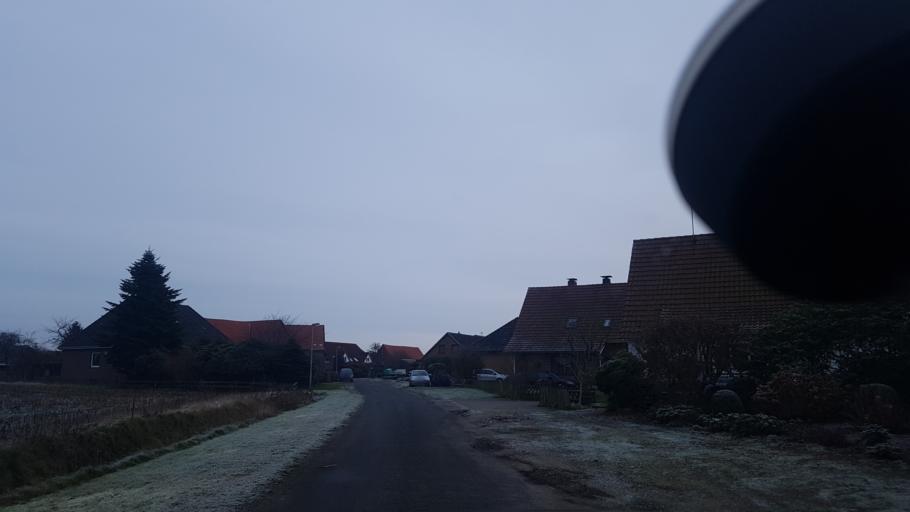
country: DE
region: Lower Saxony
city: Elmlohe
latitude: 53.6094
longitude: 8.6774
